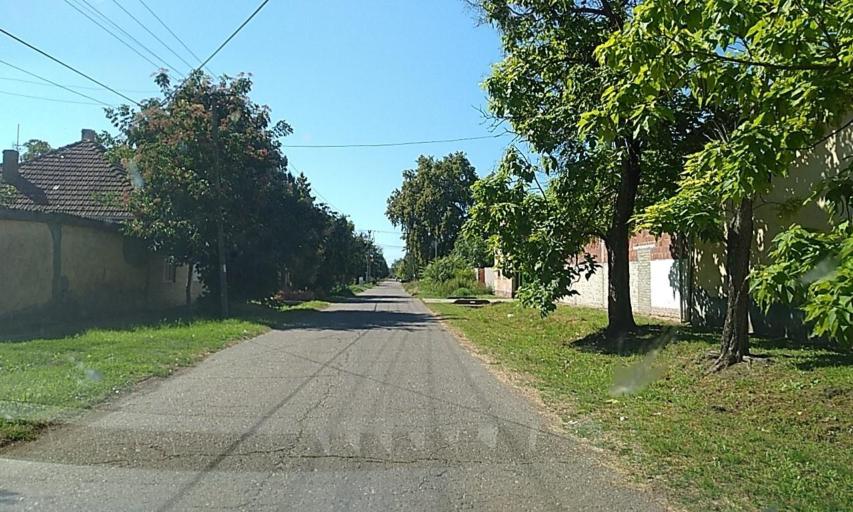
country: RS
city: Backo Gradiste
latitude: 45.5336
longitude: 20.0264
